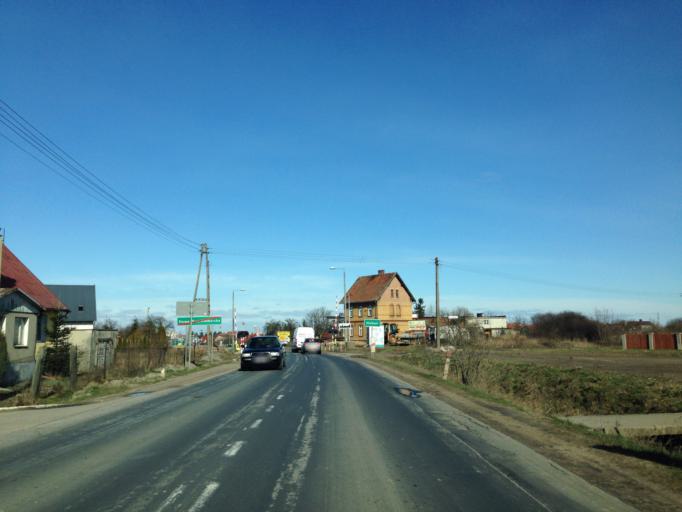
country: PL
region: Pomeranian Voivodeship
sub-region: Powiat malborski
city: Malbork
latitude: 54.0199
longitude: 19.0567
